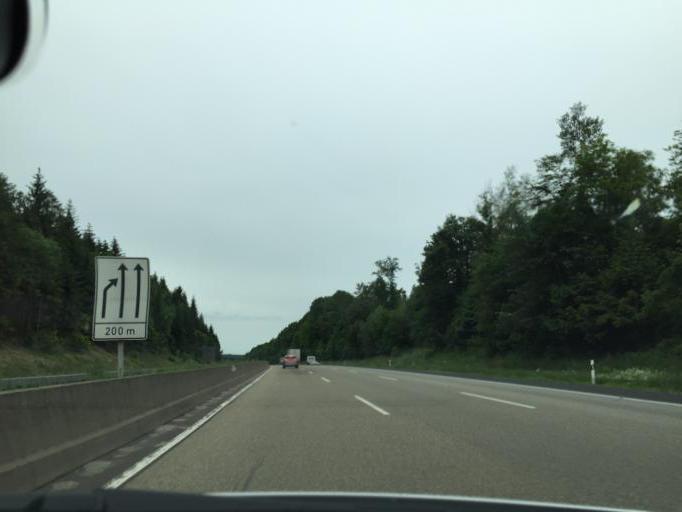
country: DE
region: Bavaria
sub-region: Regierungsbezirk Unterfranken
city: Motten
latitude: 50.3721
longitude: 9.7325
